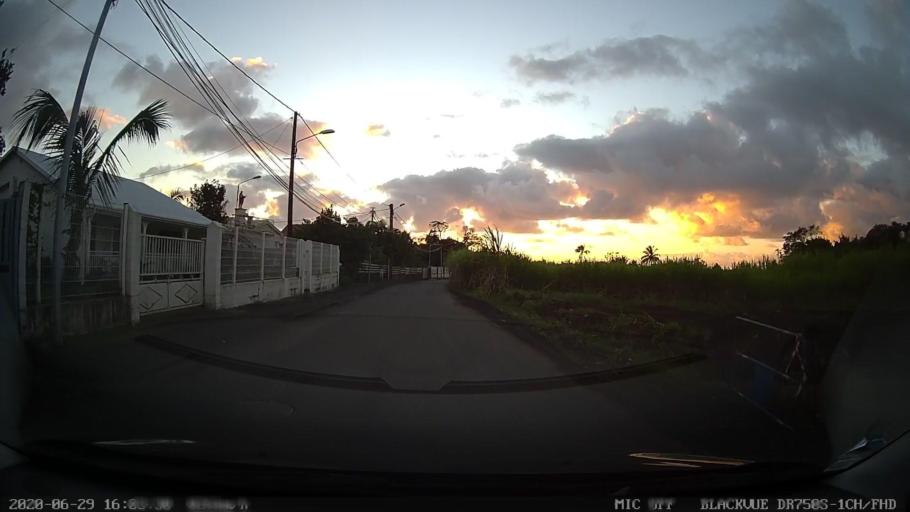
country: RE
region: Reunion
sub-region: Reunion
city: Bras-Panon
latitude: -20.9922
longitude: 55.6808
